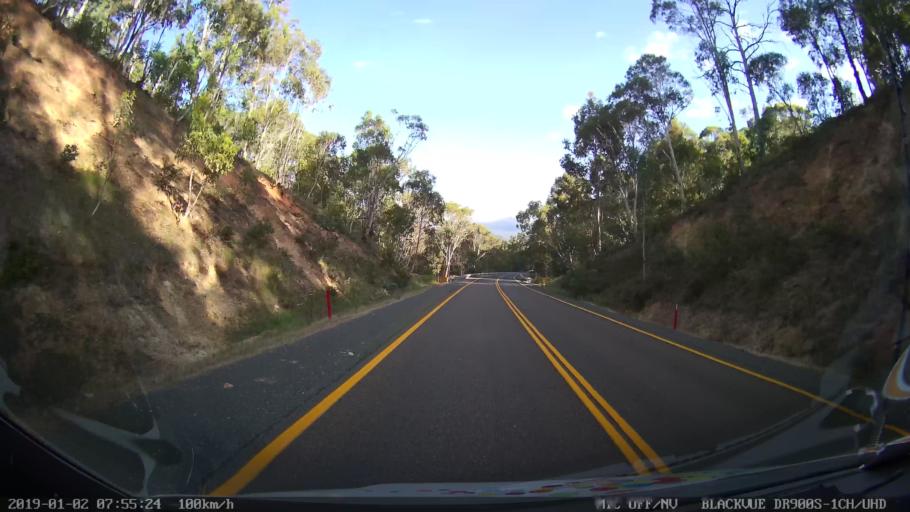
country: AU
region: New South Wales
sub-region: Tumut Shire
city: Tumut
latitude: -35.6854
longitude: 148.4871
